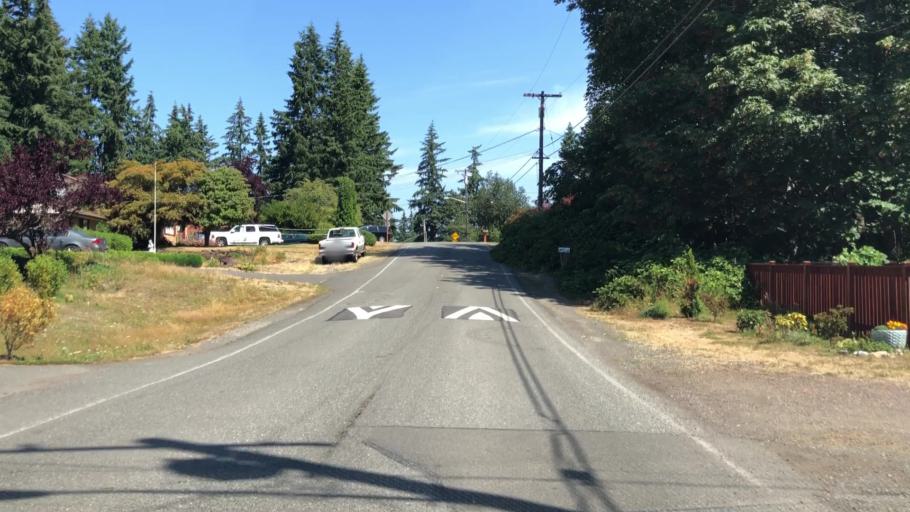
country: US
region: Washington
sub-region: King County
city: Inglewood-Finn Hill
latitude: 47.7370
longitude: -122.2410
